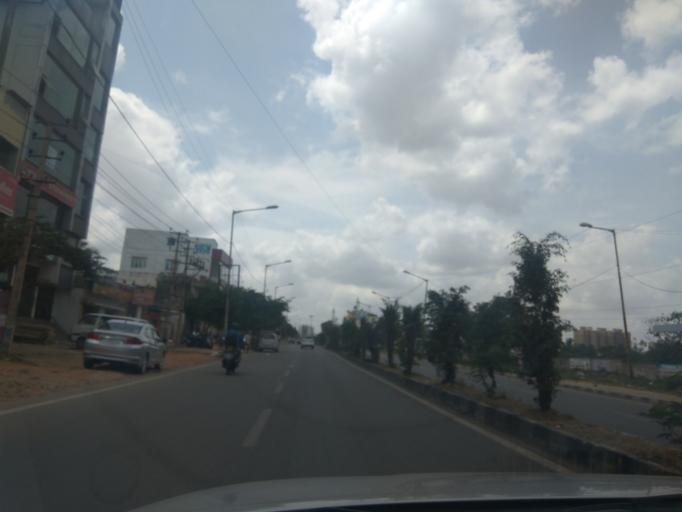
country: IN
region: Karnataka
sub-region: Bangalore Urban
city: Yelahanka
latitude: 13.0686
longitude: 77.6336
